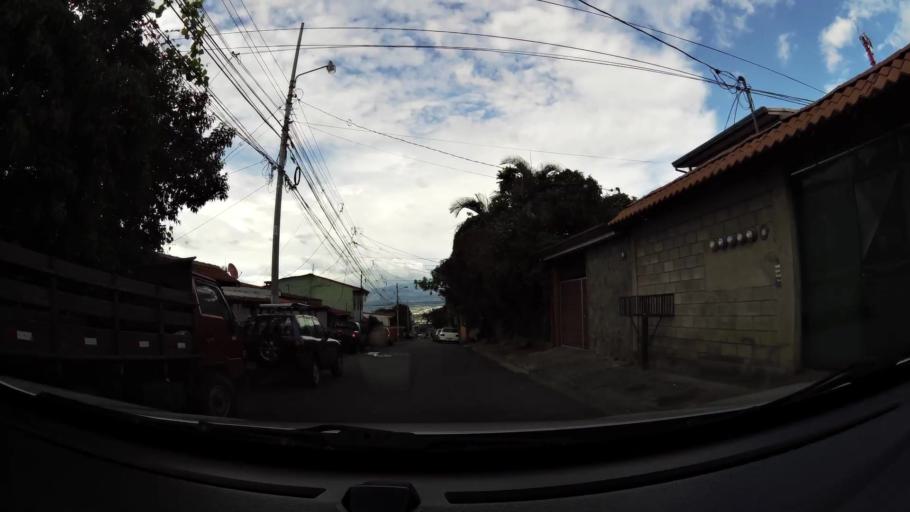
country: CR
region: San Jose
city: Escazu
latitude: 9.9164
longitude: -84.1411
